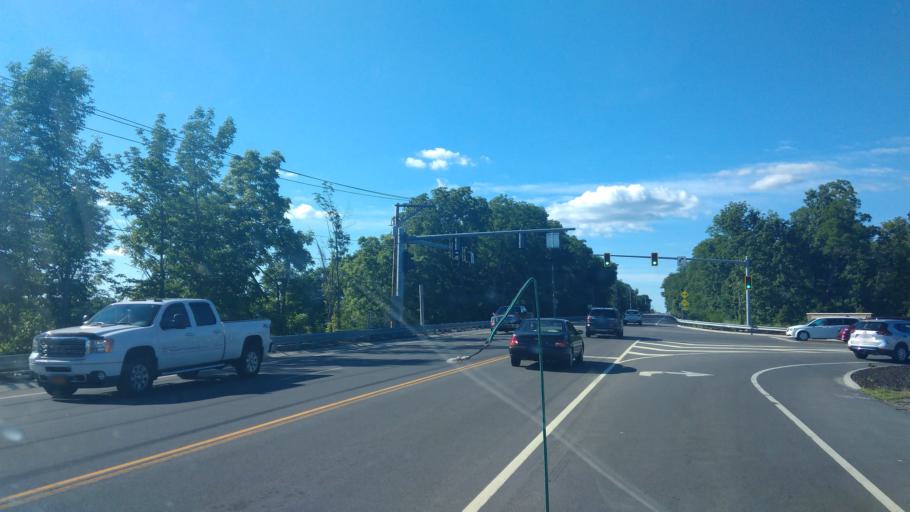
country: US
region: New York
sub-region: Seneca County
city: Waterloo
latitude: 42.9704
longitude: -76.8477
